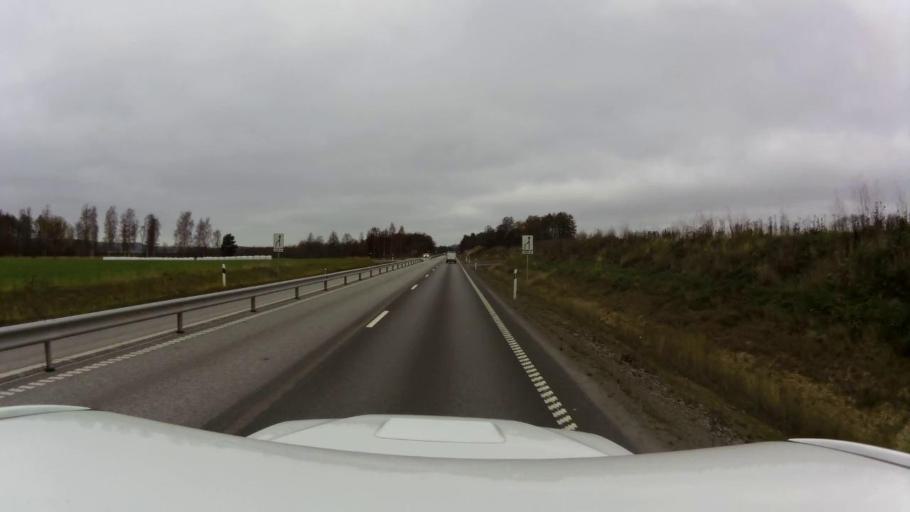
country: SE
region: OEstergoetland
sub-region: Kinda Kommun
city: Rimforsa
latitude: 58.1466
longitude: 15.6807
